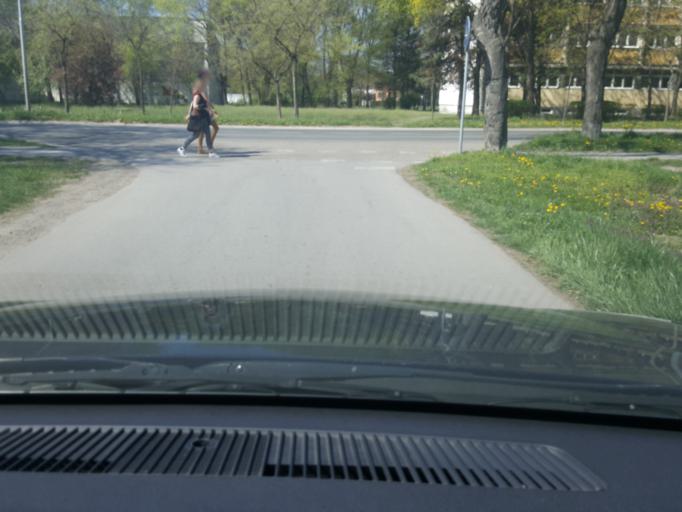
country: RS
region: Autonomna Pokrajina Vojvodina
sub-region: Zapadnobacki Okrug
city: Sombor
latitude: 45.7627
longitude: 19.1023
